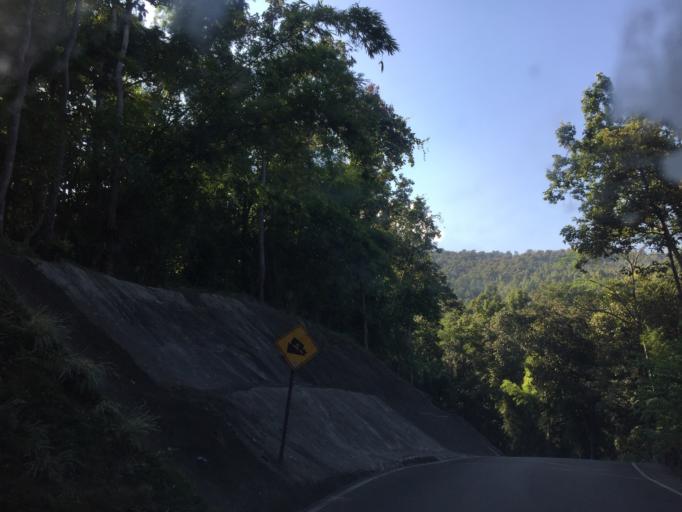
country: TH
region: Chiang Mai
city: Chiang Mai
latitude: 18.8029
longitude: 98.9436
